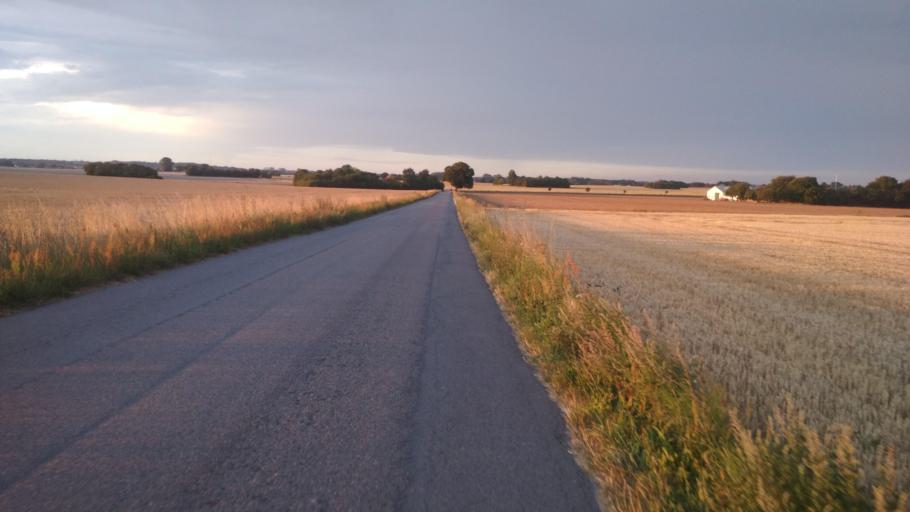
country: DK
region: Capital Region
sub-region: Bornholm Kommune
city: Akirkeby
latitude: 55.0302
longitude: 14.9125
